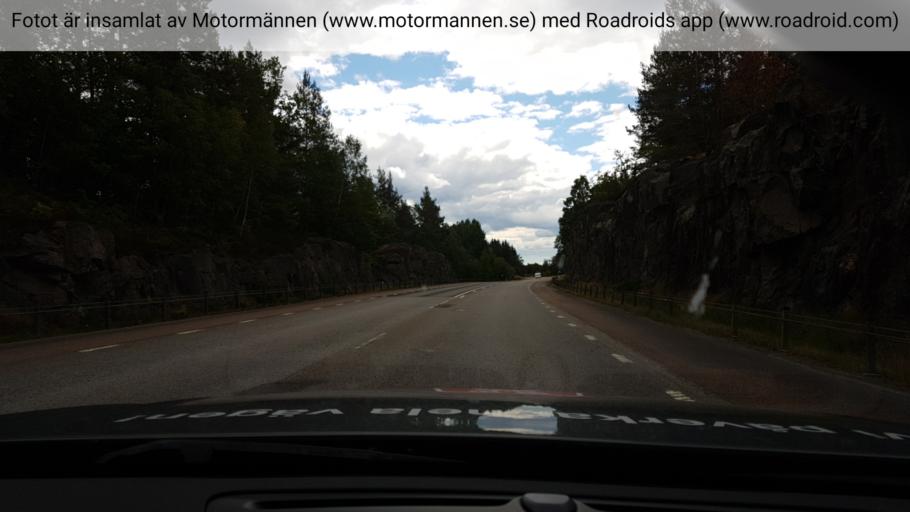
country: SE
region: Kalmar
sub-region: Vasterviks Kommun
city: Ankarsrum
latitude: 57.6477
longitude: 16.4431
